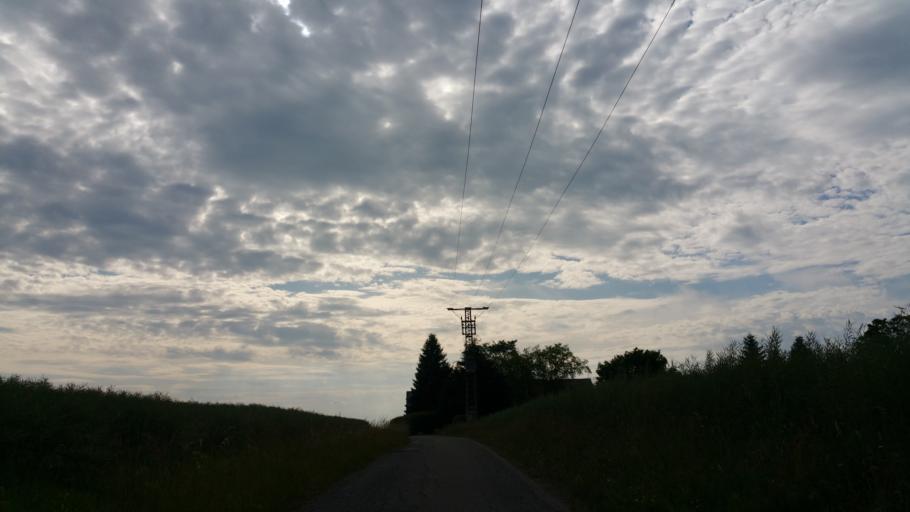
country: DE
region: Bavaria
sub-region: Upper Franconia
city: Schwarzenbach an der Saale
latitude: 50.2032
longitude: 11.9347
